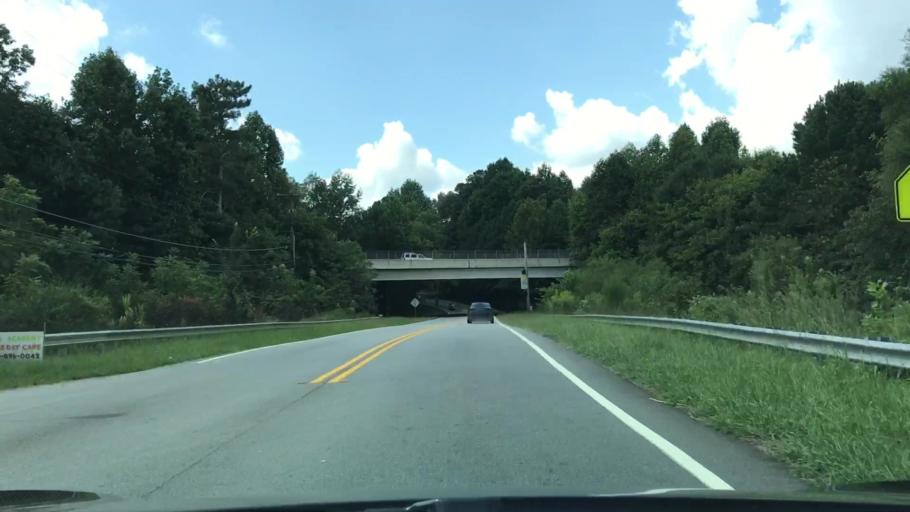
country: US
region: Georgia
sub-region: Gwinnett County
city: Snellville
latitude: 33.8967
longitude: -84.0665
